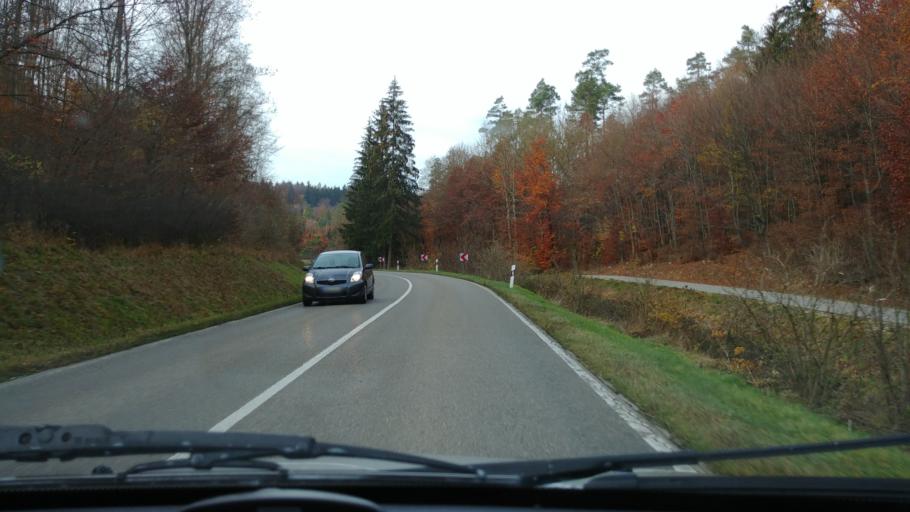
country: DE
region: Baden-Wuerttemberg
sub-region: Regierungsbezirk Stuttgart
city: Herbrechtingen
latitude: 48.6643
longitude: 10.2022
